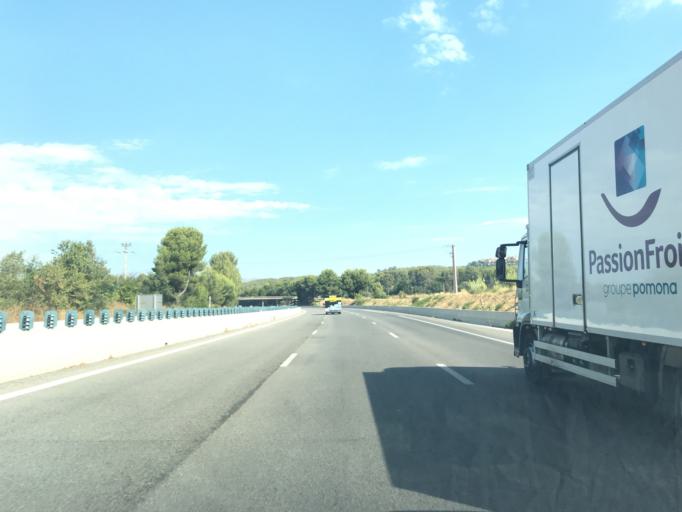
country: FR
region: Provence-Alpes-Cote d'Azur
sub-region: Departement du Var
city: Le Castellet
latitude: 43.1824
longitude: 5.7698
